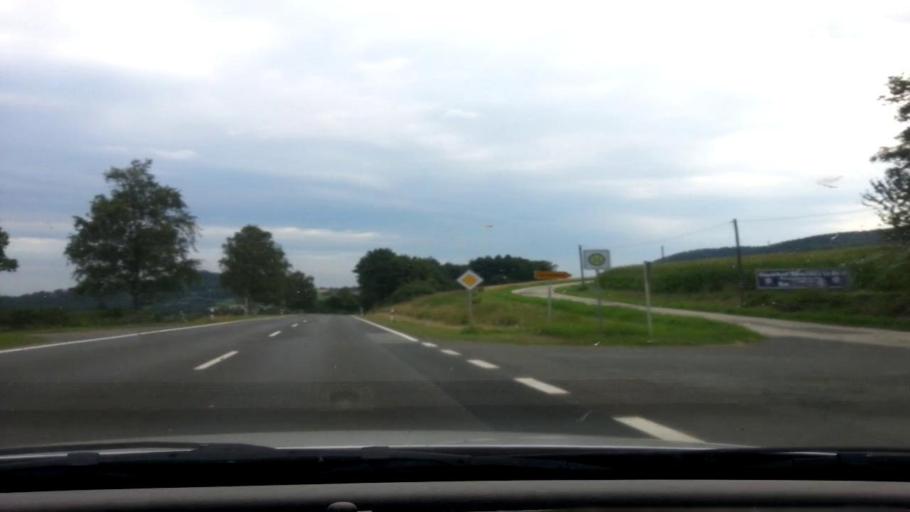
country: DE
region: Bavaria
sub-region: Upper Palatinate
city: Kastl
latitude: 49.8562
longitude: 11.9689
